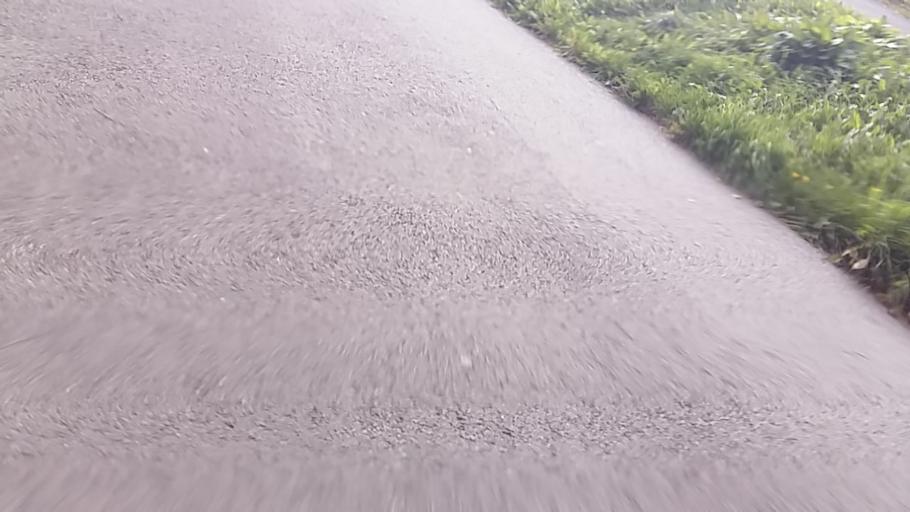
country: SE
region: Joenkoeping
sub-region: Jonkopings Kommun
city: Odensjo
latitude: 57.7366
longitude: 14.1515
